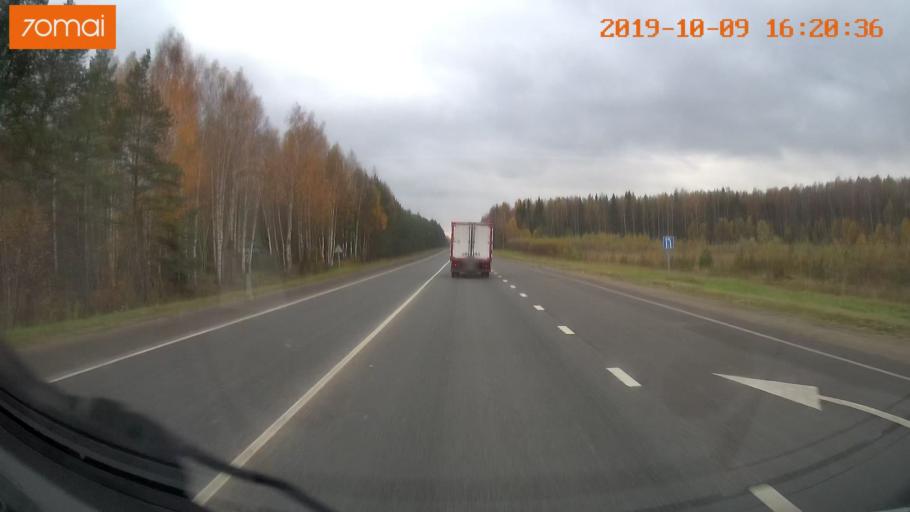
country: RU
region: Kostroma
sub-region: Kostromskoy Rayon
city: Kostroma
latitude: 57.7043
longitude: 40.8917
